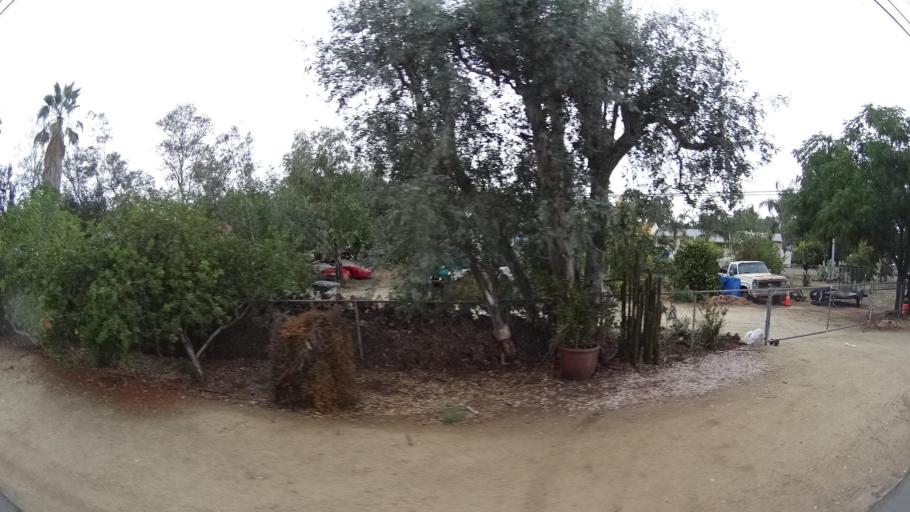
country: US
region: California
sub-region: San Diego County
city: Ramona
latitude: 33.0243
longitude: -116.8795
